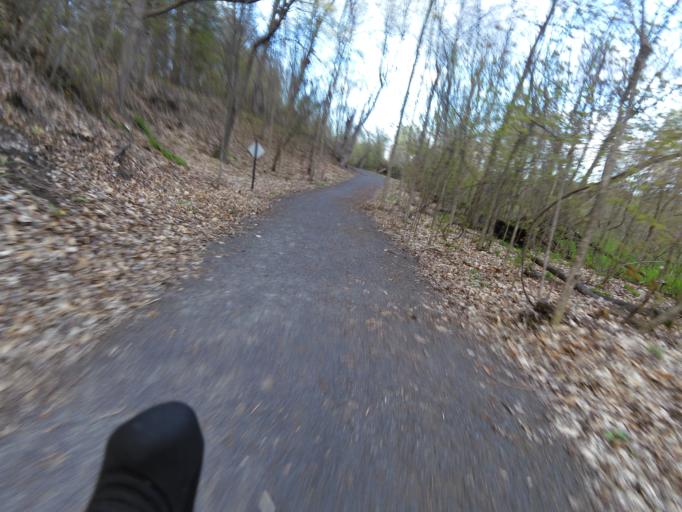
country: CA
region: Ontario
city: Ottawa
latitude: 45.3183
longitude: -75.7103
